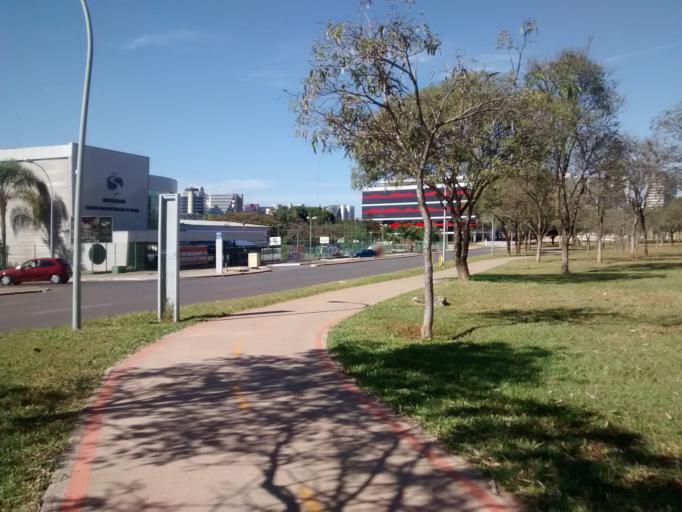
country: BR
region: Federal District
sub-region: Brasilia
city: Brasilia
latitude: -15.7813
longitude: -47.8907
